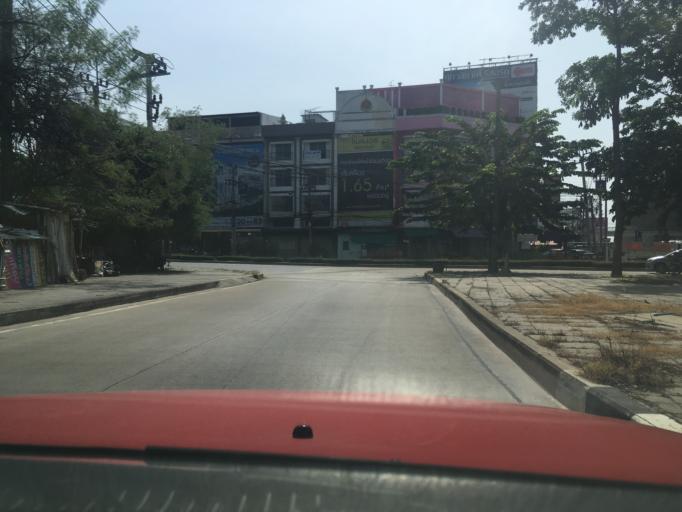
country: TH
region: Nonthaburi
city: Mueang Nonthaburi
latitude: 13.8711
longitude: 100.4816
